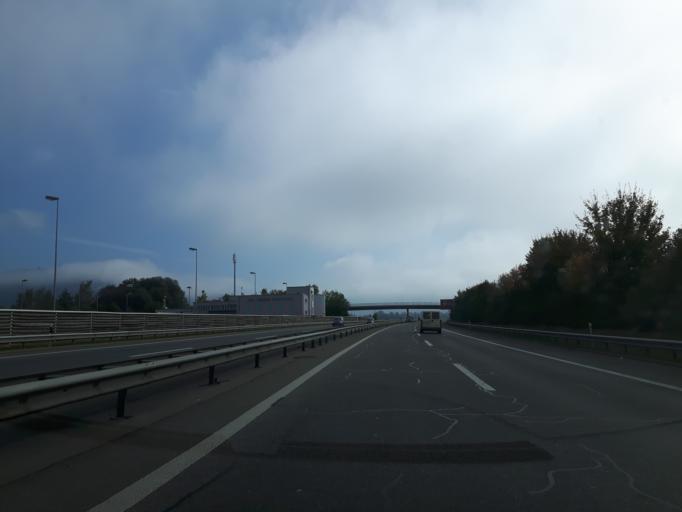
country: CH
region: Lucerne
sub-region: Willisau District
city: Reiden
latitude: 47.2318
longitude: 7.9697
